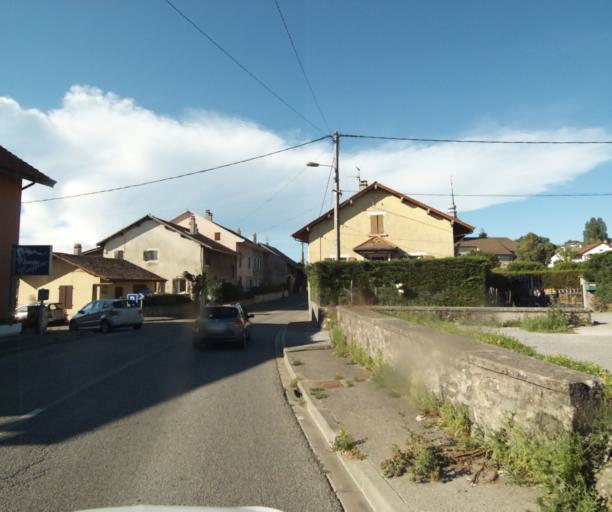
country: FR
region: Rhone-Alpes
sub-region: Departement de la Haute-Savoie
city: Loisin
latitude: 46.2915
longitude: 6.3092
